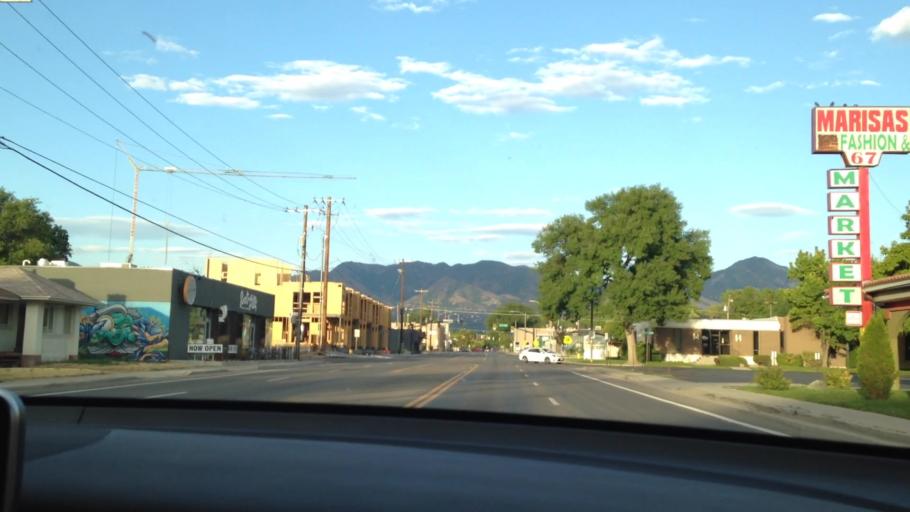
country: US
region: Utah
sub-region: Salt Lake County
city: South Salt Lake
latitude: 40.7335
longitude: -111.8936
